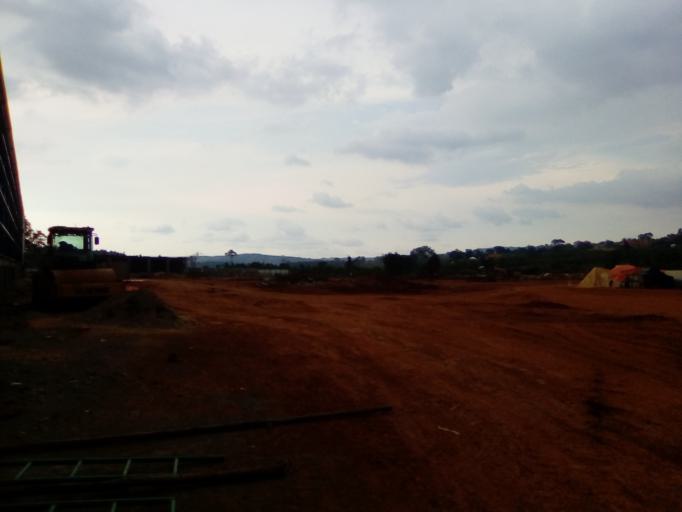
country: UG
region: Central Region
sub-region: Wakiso District
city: Kajansi
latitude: 0.1666
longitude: 32.5127
